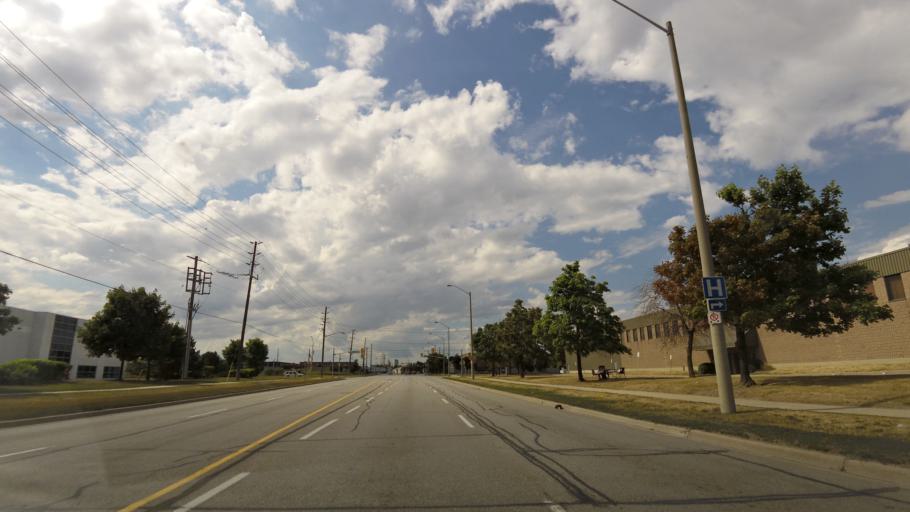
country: CA
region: Ontario
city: Brampton
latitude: 43.6883
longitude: -79.7037
